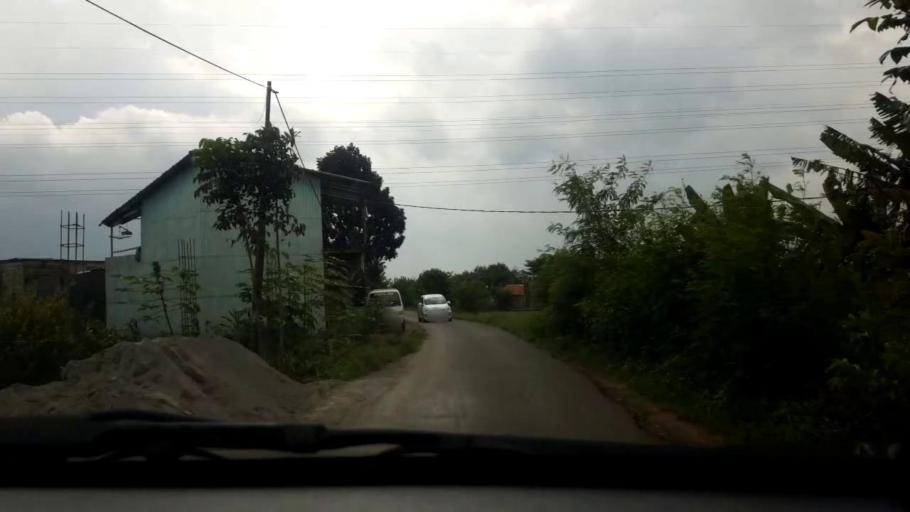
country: ID
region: West Java
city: Cileunyi
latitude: -6.9552
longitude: 107.7133
